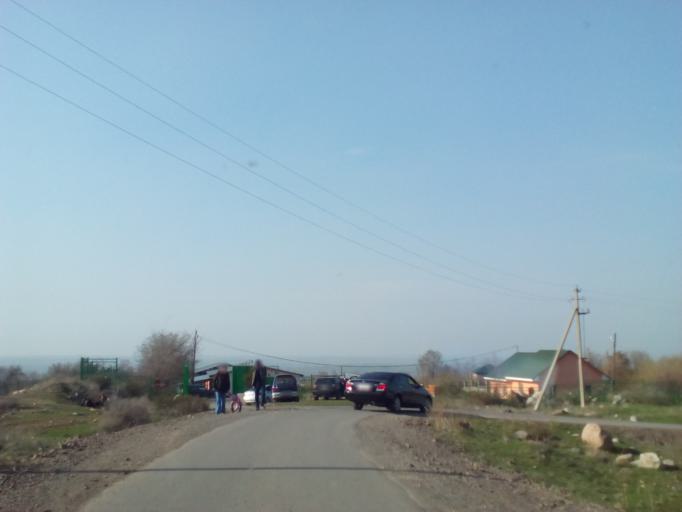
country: KZ
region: Almaty Oblysy
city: Burunday
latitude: 43.1512
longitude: 76.5726
